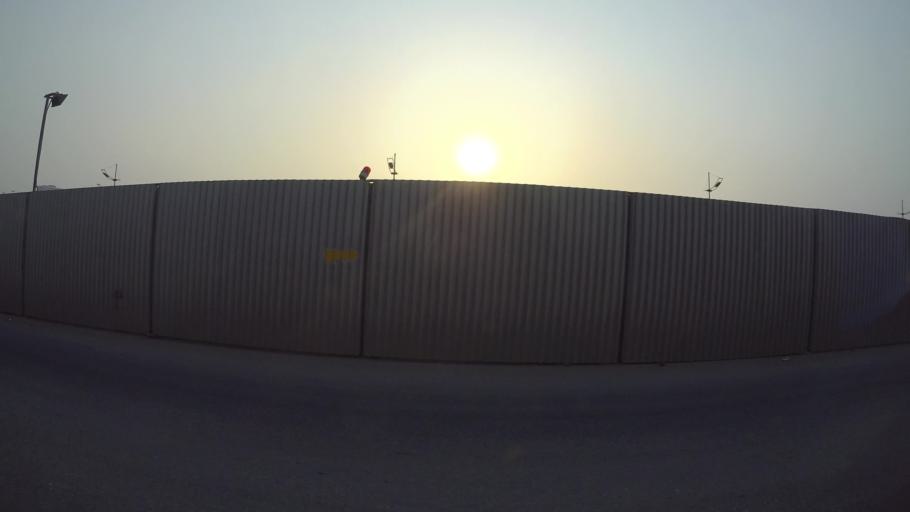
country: VN
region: Ha Noi
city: Tay Ho
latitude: 21.0737
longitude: 105.7858
